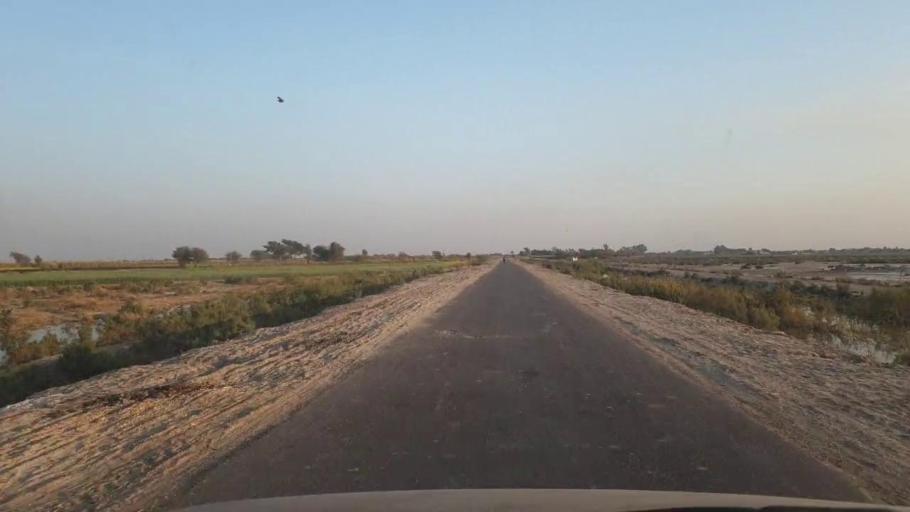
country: PK
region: Sindh
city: Chambar
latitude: 25.2849
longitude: 68.9097
